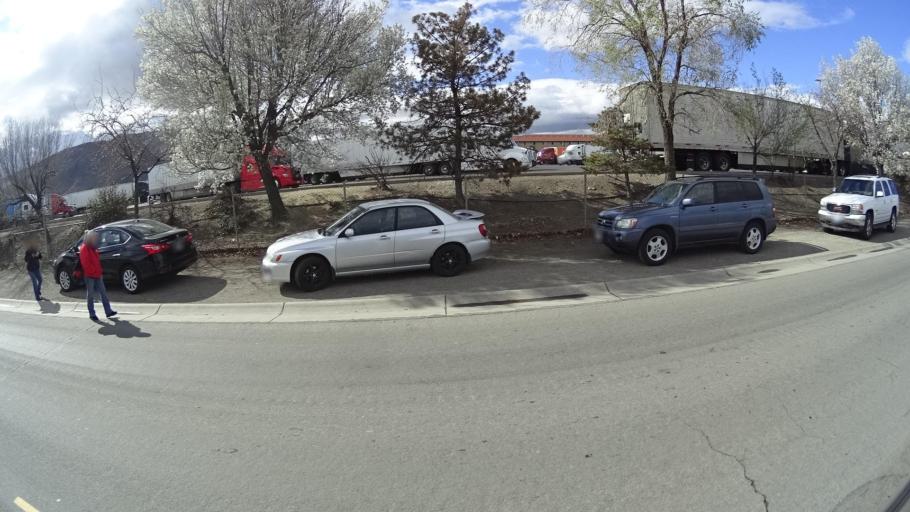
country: US
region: Nevada
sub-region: Washoe County
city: Sparks
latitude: 39.5251
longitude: -119.7086
